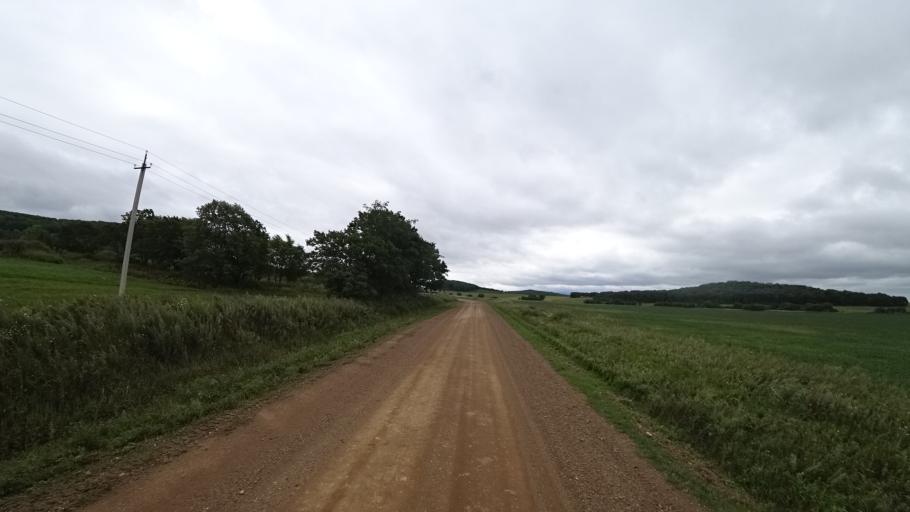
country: RU
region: Primorskiy
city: Chernigovka
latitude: 44.4724
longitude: 132.5811
